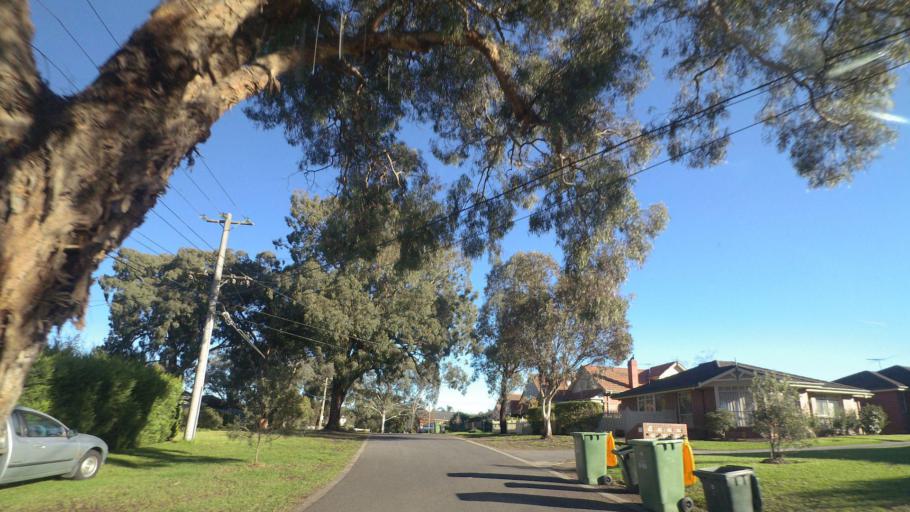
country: AU
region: Victoria
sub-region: Banyule
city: Yallambie
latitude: -37.7310
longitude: 145.1012
